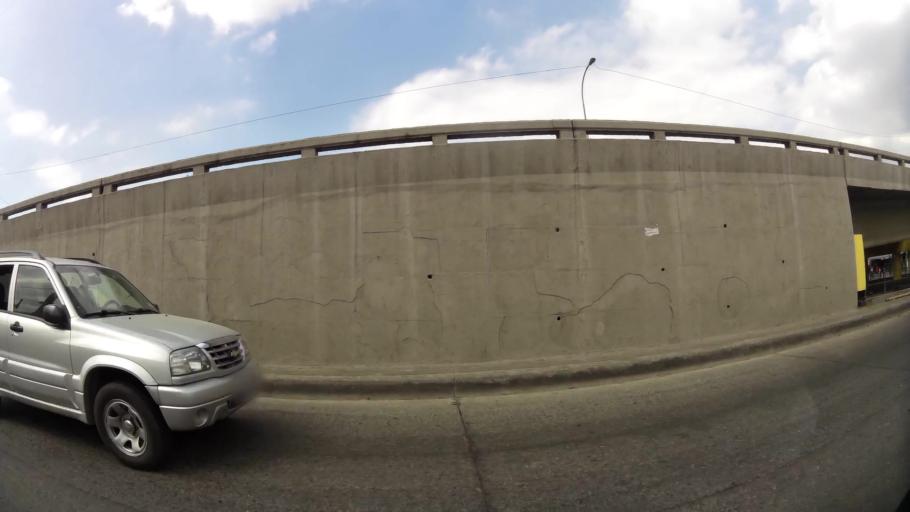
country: EC
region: Guayas
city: Santa Lucia
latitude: -2.0986
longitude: -79.9361
